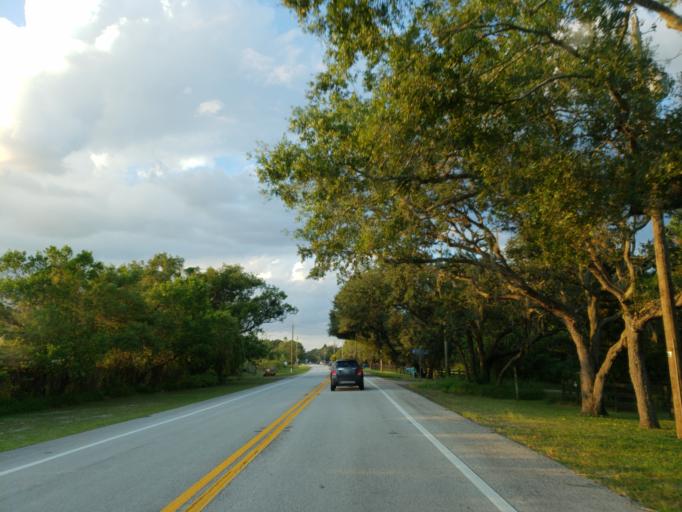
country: US
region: Florida
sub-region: Pasco County
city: Odessa
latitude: 28.1633
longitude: -82.5883
